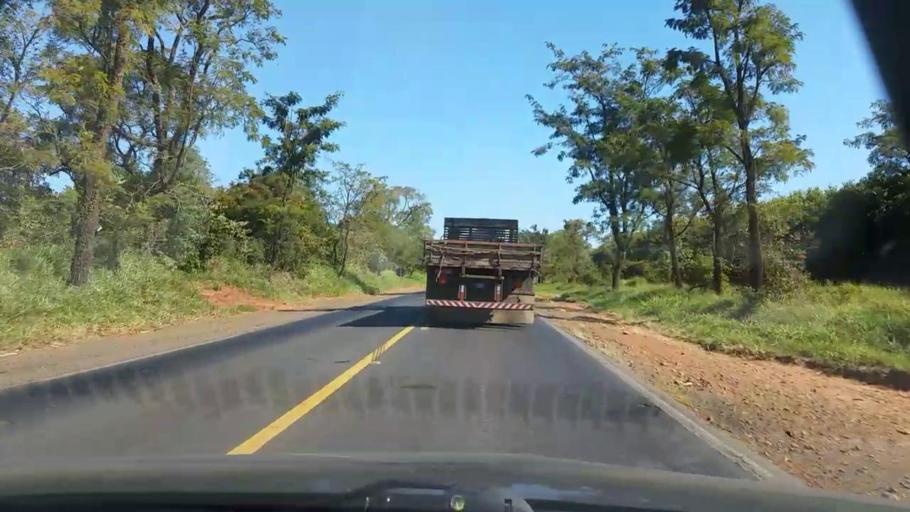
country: BR
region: Sao Paulo
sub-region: Sao Manuel
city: Sao Manuel
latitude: -22.8135
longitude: -48.6795
